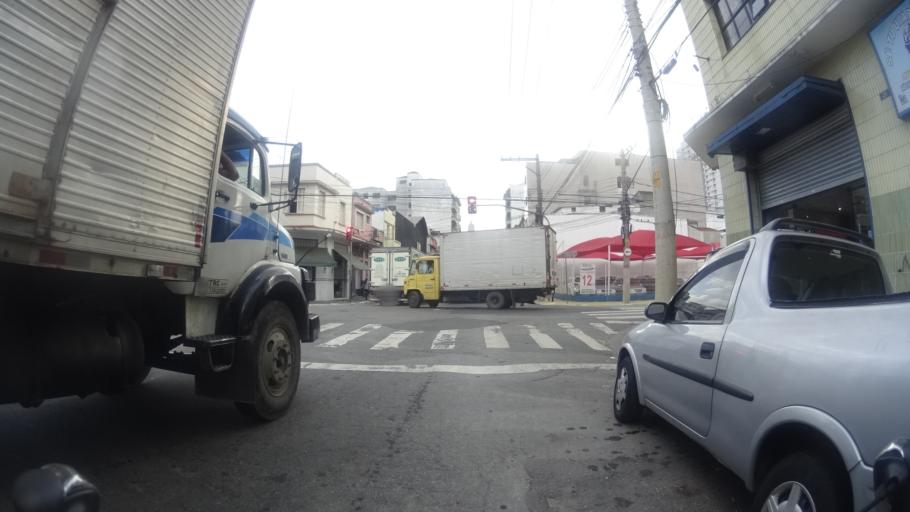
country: BR
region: Sao Paulo
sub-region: Sao Paulo
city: Sao Paulo
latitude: -23.5432
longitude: -46.6235
